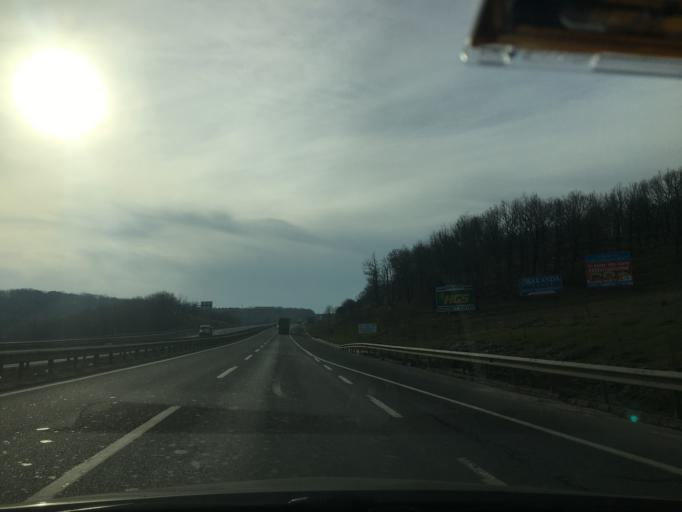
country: TR
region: Tekirdag
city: Cerkezkoey
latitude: 41.2735
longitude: 28.0281
